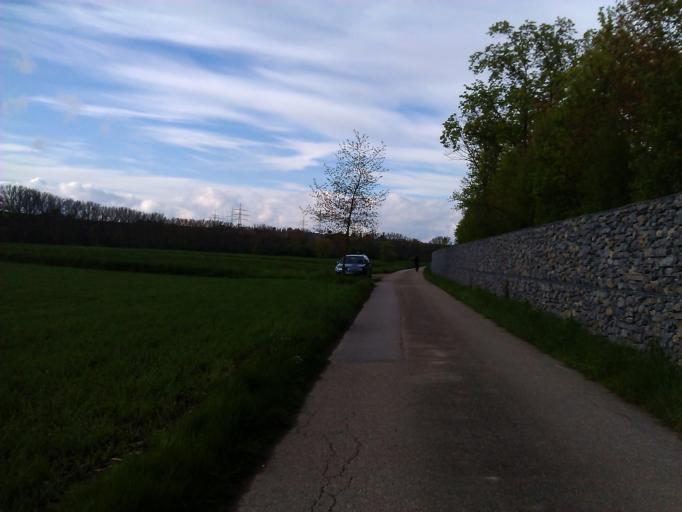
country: DE
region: Baden-Wuerttemberg
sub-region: Regierungsbezirk Stuttgart
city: Nordheim
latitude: 49.1035
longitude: 9.1523
